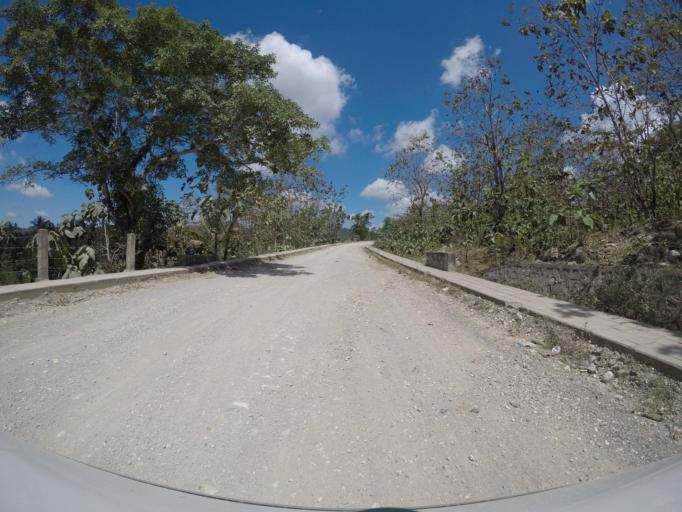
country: TL
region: Viqueque
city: Viqueque
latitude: -8.8443
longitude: 126.3695
